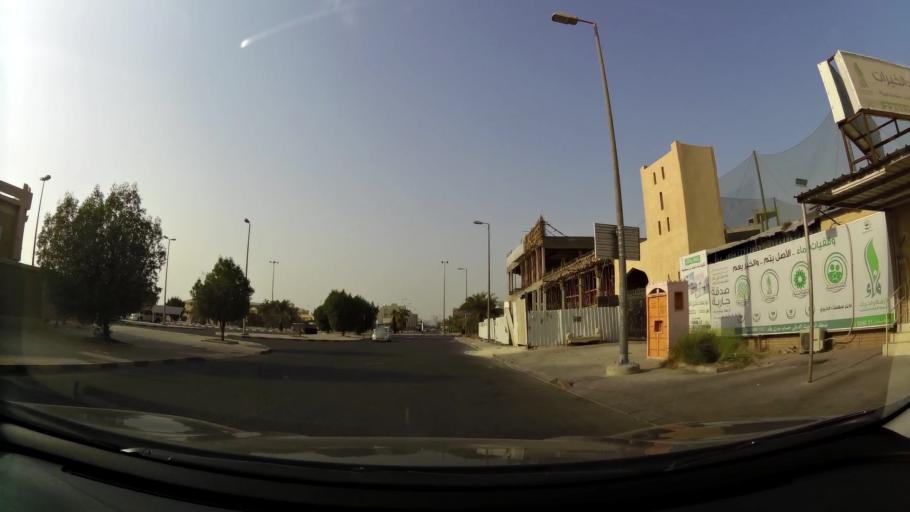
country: KW
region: Muhafazat Hawalli
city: Hawalli
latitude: 29.3301
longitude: 48.0050
